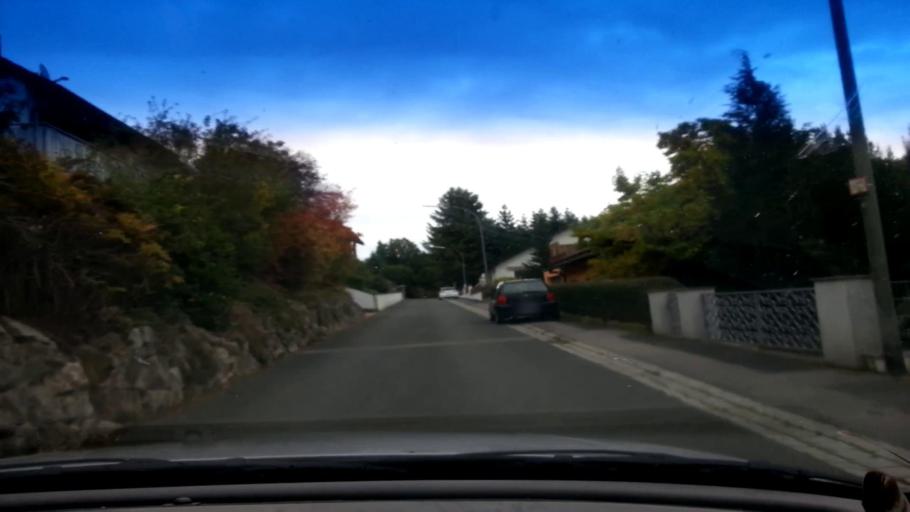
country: DE
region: Bavaria
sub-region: Upper Franconia
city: Priesendorf
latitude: 49.9035
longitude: 10.7168
